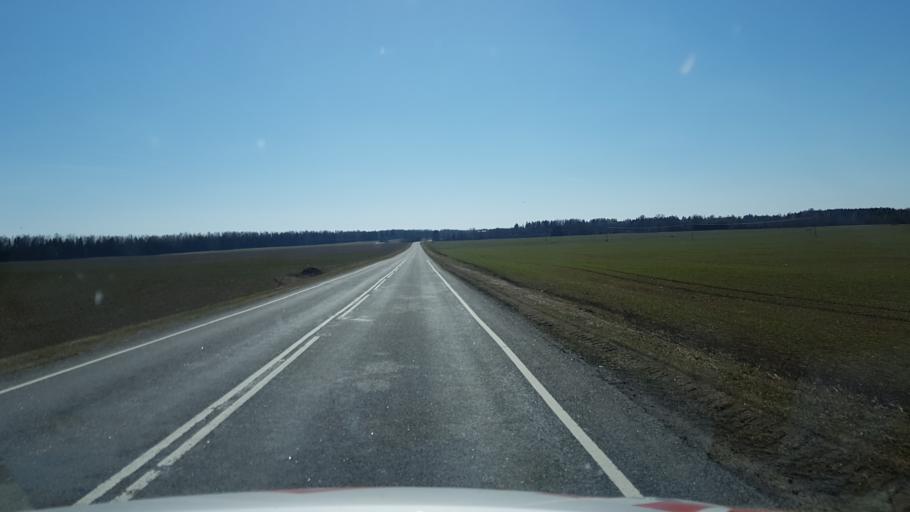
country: EE
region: Laeaene-Virumaa
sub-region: Tamsalu vald
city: Tamsalu
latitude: 59.1233
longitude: 26.0307
